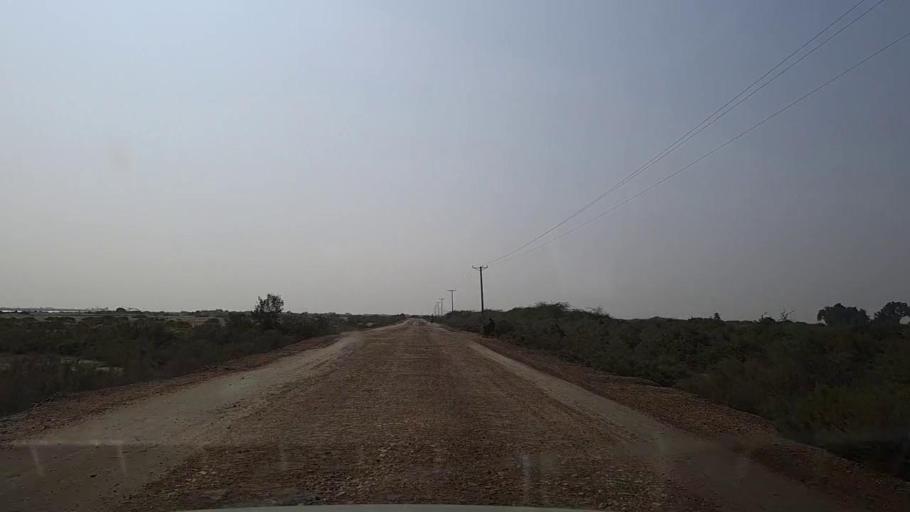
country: PK
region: Sindh
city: Mirpur Sakro
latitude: 24.5370
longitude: 67.5976
